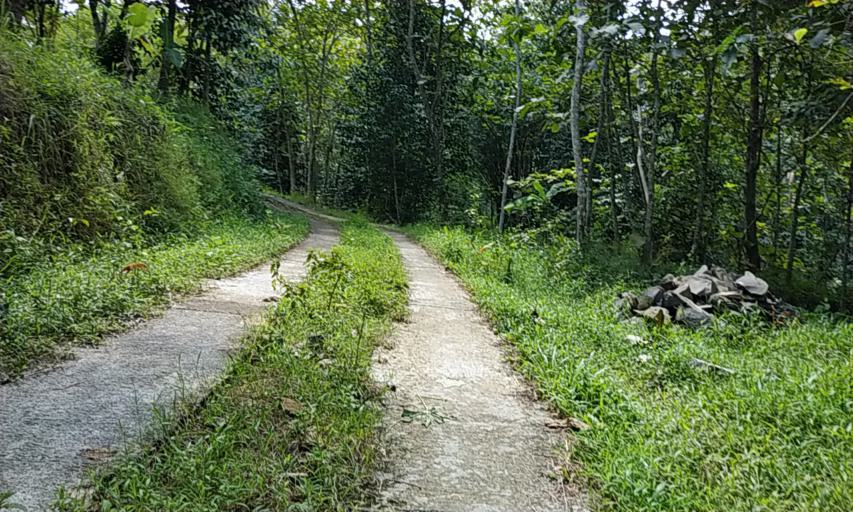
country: ID
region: Central Java
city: Kutoarjo
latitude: -7.6185
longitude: 109.7256
